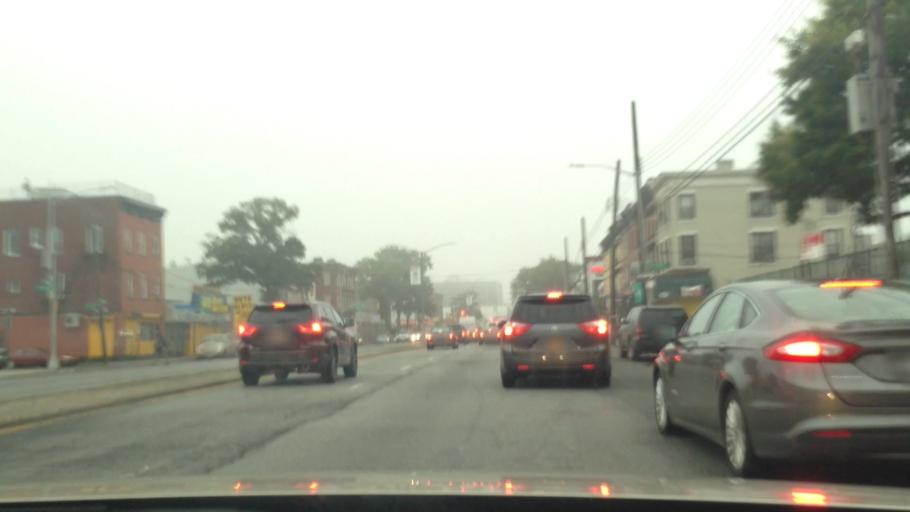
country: US
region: New York
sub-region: Kings County
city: East New York
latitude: 40.6766
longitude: -73.8907
